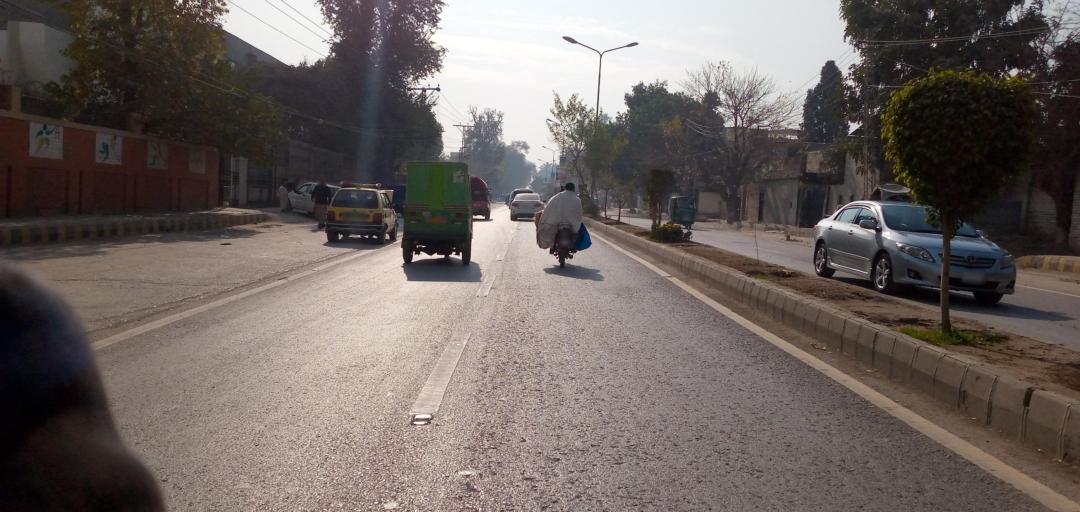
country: PK
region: Khyber Pakhtunkhwa
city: Peshawar
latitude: 33.9927
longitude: 71.5336
